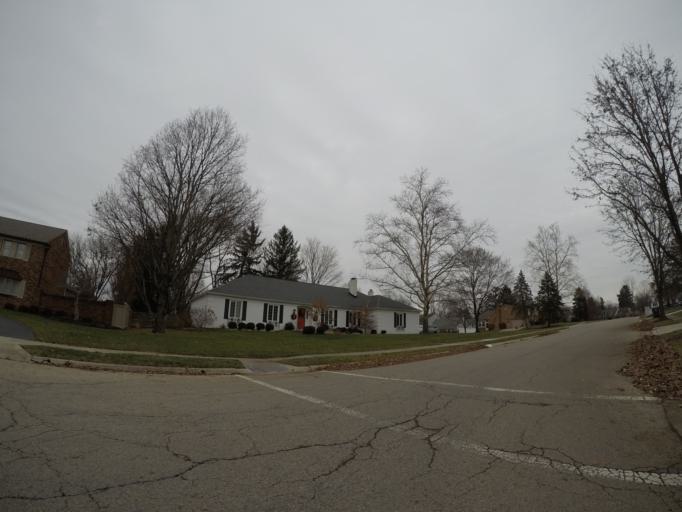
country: US
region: Ohio
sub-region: Franklin County
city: Dublin
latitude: 40.0485
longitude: -83.0878
